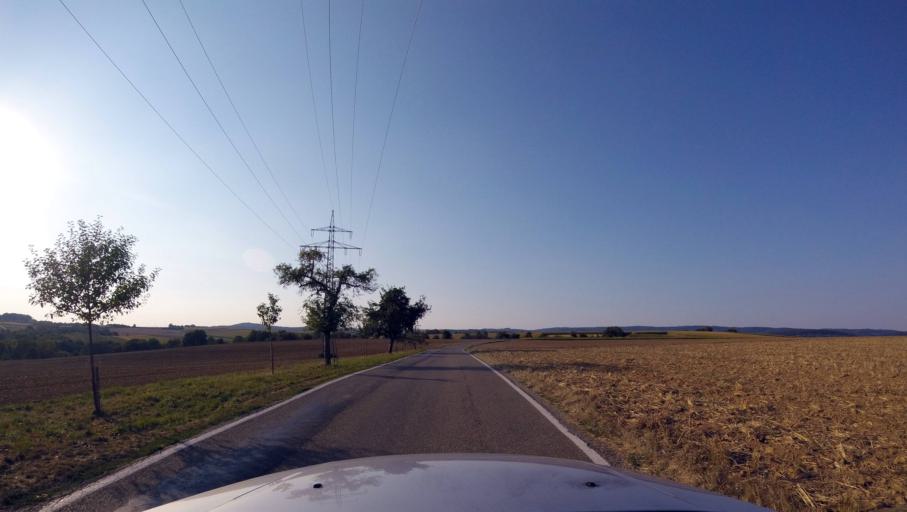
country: DE
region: Baden-Wuerttemberg
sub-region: Regierungsbezirk Stuttgart
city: Mittelschontal
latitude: 48.9513
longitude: 9.4010
